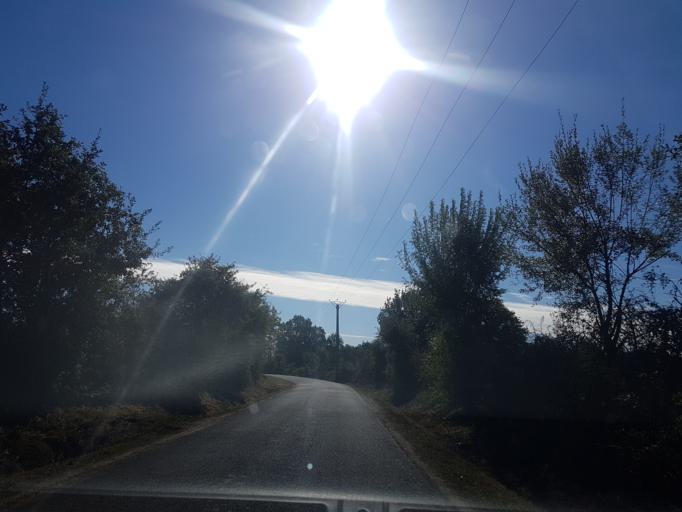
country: FR
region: Pays de la Loire
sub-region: Departement de la Loire-Atlantique
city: Petit-Mars
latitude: 47.3934
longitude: -1.4643
